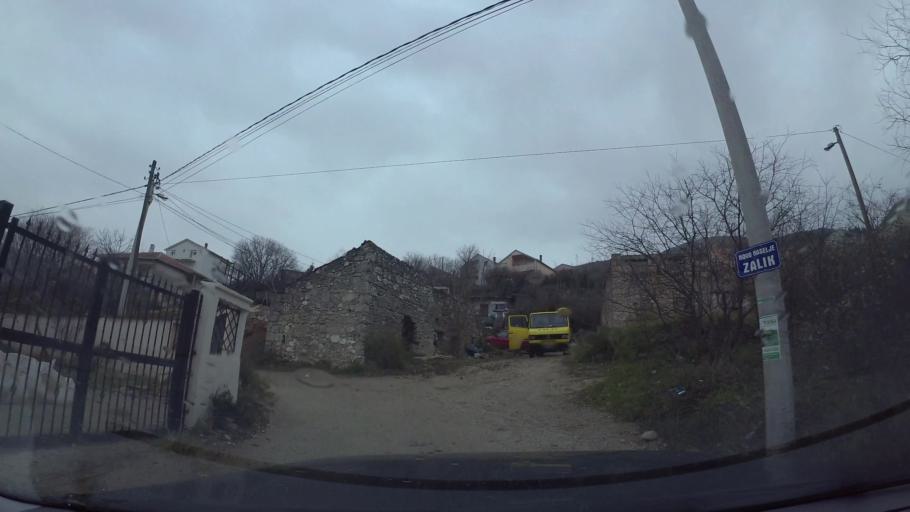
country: BA
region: Federation of Bosnia and Herzegovina
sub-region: Hercegovacko-Bosanski Kanton
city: Mostar
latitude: 43.3549
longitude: 17.8157
